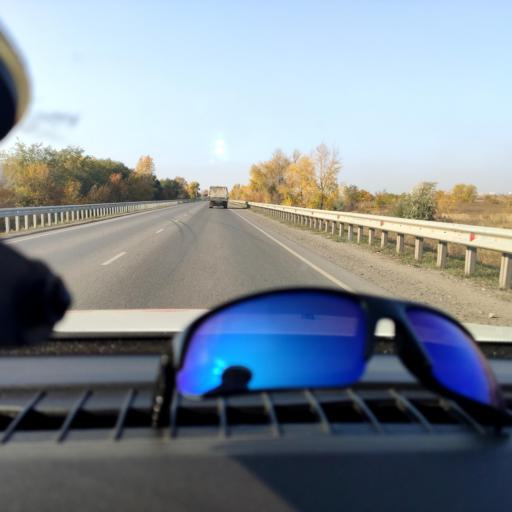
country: RU
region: Samara
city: Samara
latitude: 53.1100
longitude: 50.1310
